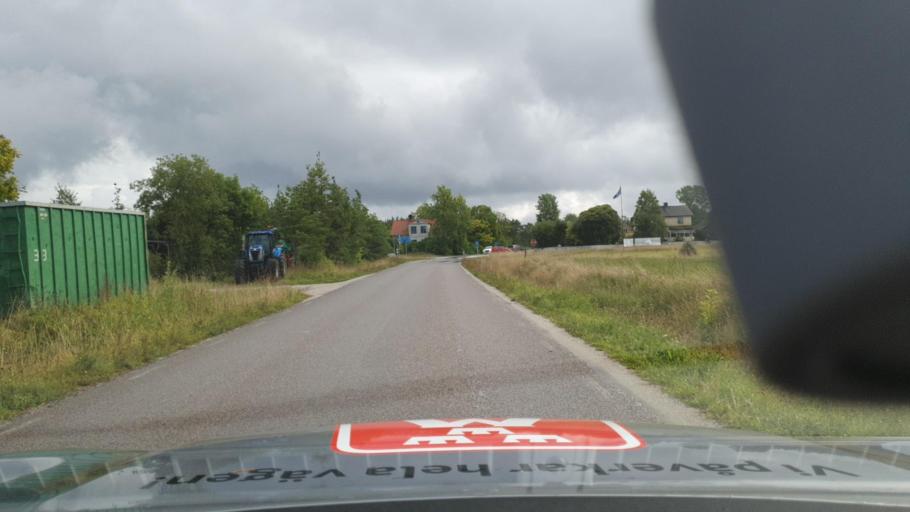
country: SE
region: Gotland
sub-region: Gotland
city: Slite
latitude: 57.6821
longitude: 18.7661
